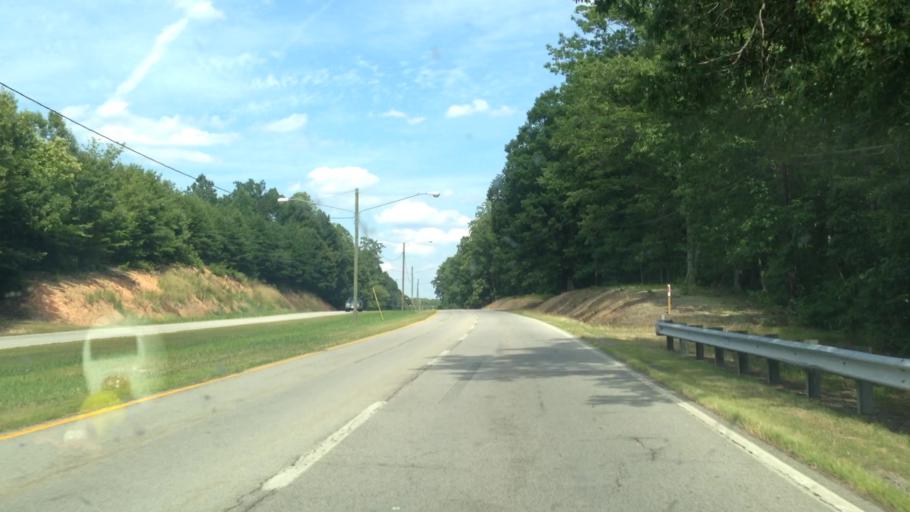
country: US
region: Virginia
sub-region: City of Danville
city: Danville
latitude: 36.5951
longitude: -79.4928
